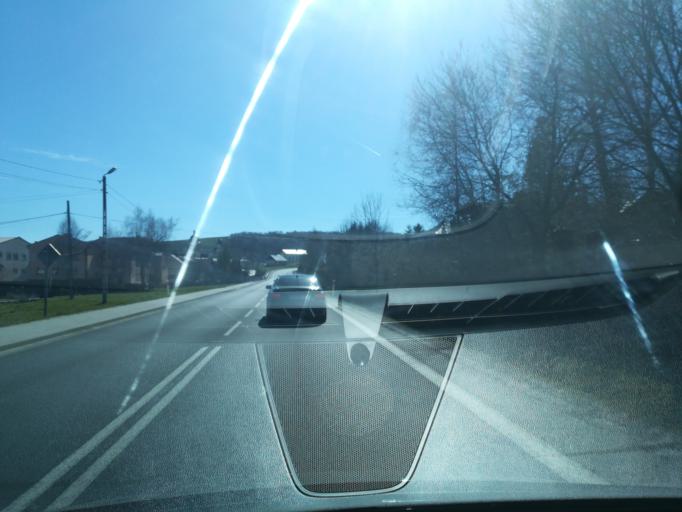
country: PL
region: Subcarpathian Voivodeship
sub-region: Powiat strzyzowski
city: Niebylec
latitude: 49.8600
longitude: 21.9034
